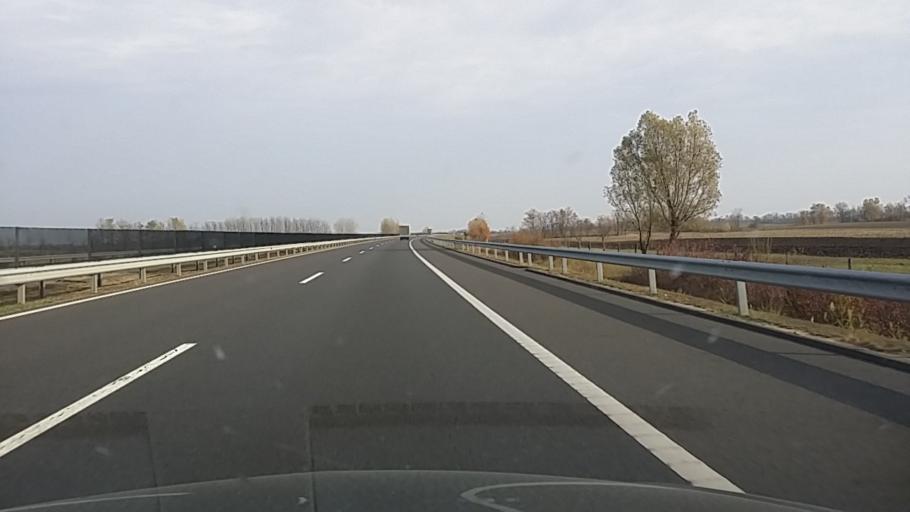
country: HU
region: Szabolcs-Szatmar-Bereg
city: Nagycserkesz
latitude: 47.9034
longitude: 21.5117
